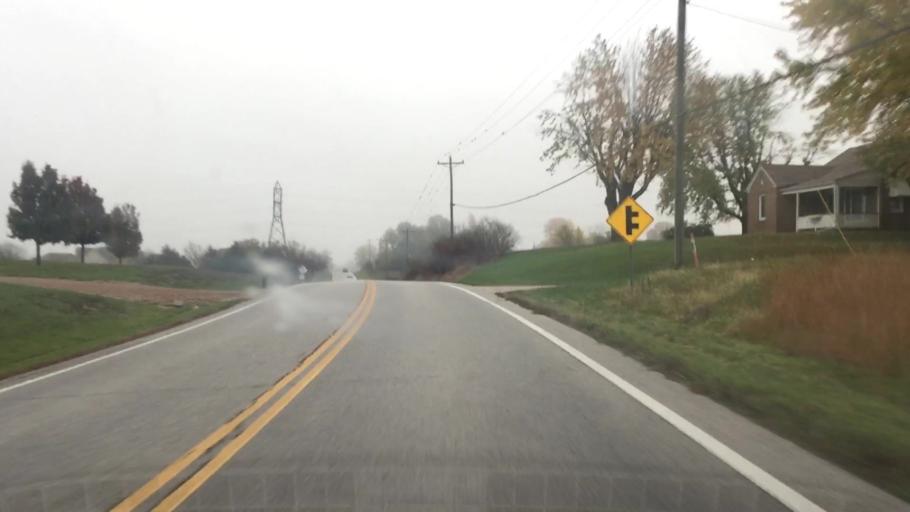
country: US
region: Missouri
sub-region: Callaway County
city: Fulton
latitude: 38.8581
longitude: -91.9951
